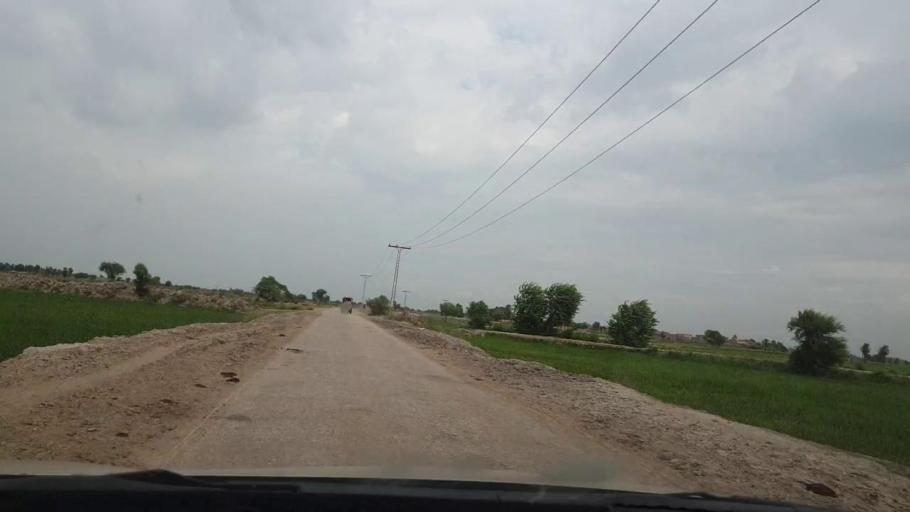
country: PK
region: Sindh
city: Ratodero
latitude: 27.8131
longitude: 68.3092
